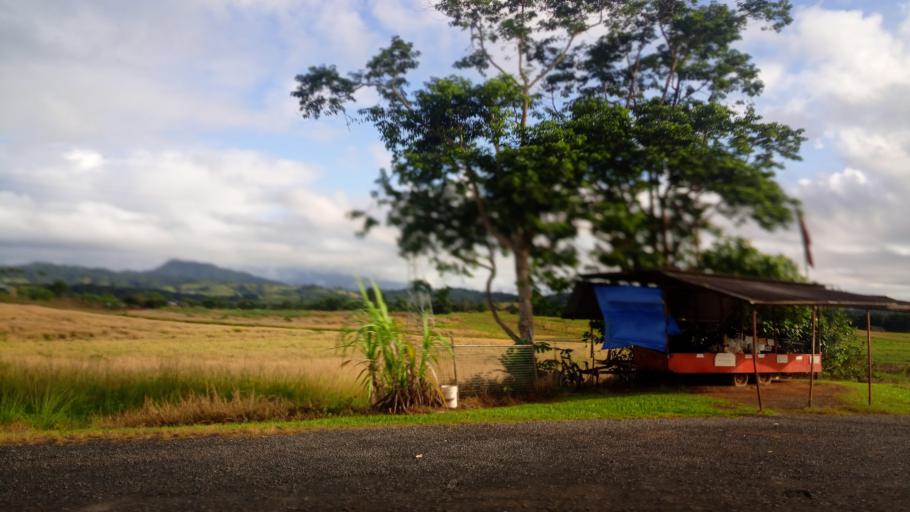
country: AU
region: Queensland
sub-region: Cassowary Coast
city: Innisfail
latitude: -17.5325
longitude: 145.9761
